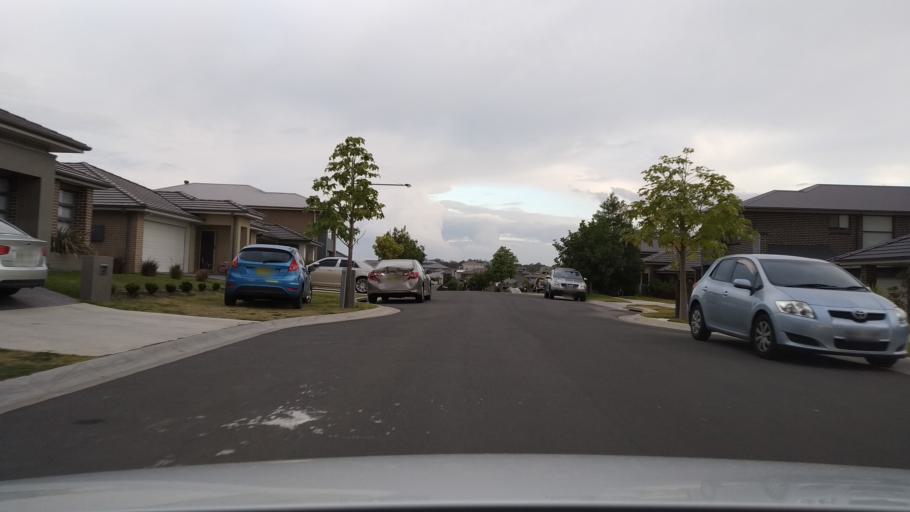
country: AU
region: New South Wales
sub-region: Camden
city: Narellan
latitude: -34.0036
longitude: 150.7278
